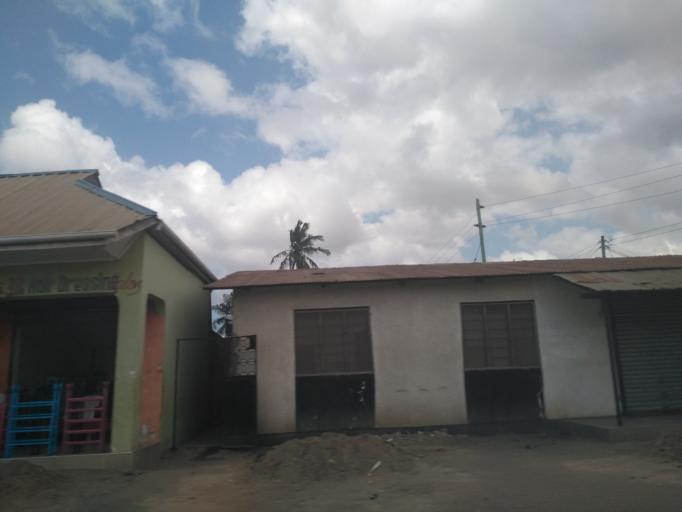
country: TZ
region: Dar es Salaam
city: Dar es Salaam
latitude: -6.8935
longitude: 39.2836
